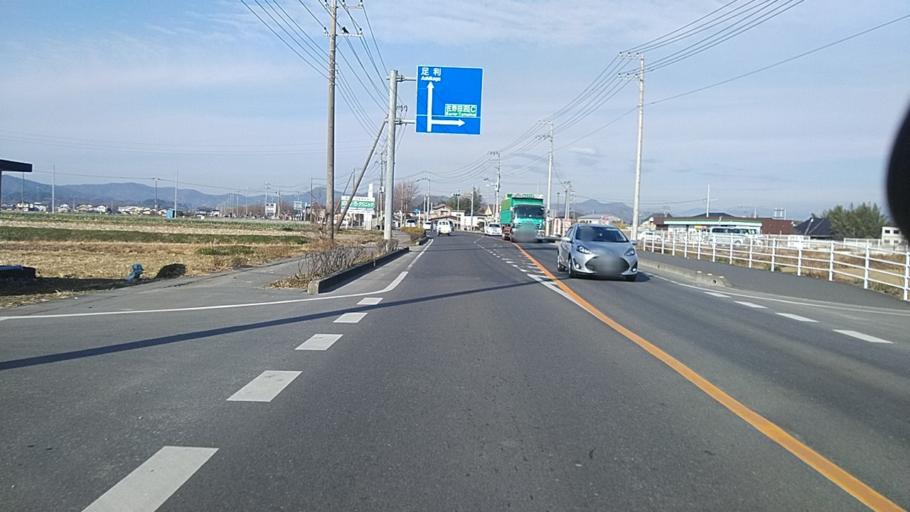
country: JP
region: Tochigi
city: Tanuma
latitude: 36.3443
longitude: 139.5694
